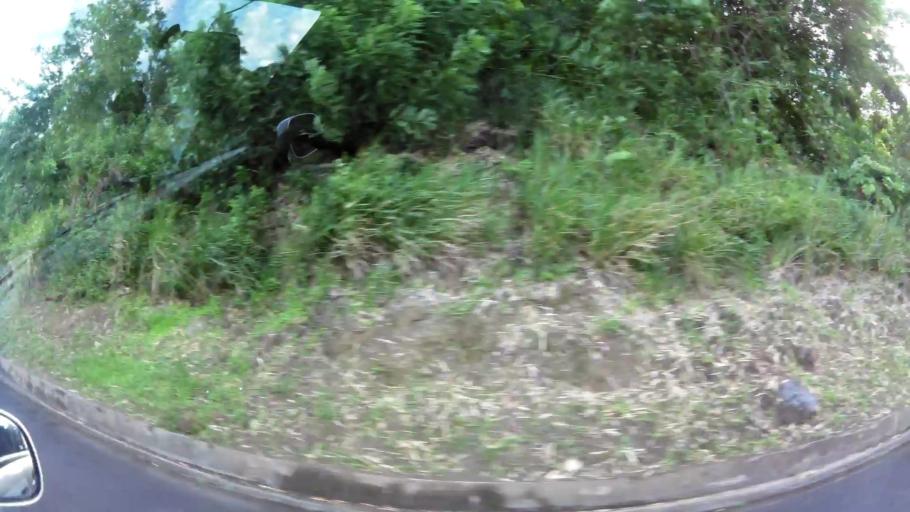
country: GD
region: Saint Mark
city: Victoria
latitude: 12.2171
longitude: -61.6885
